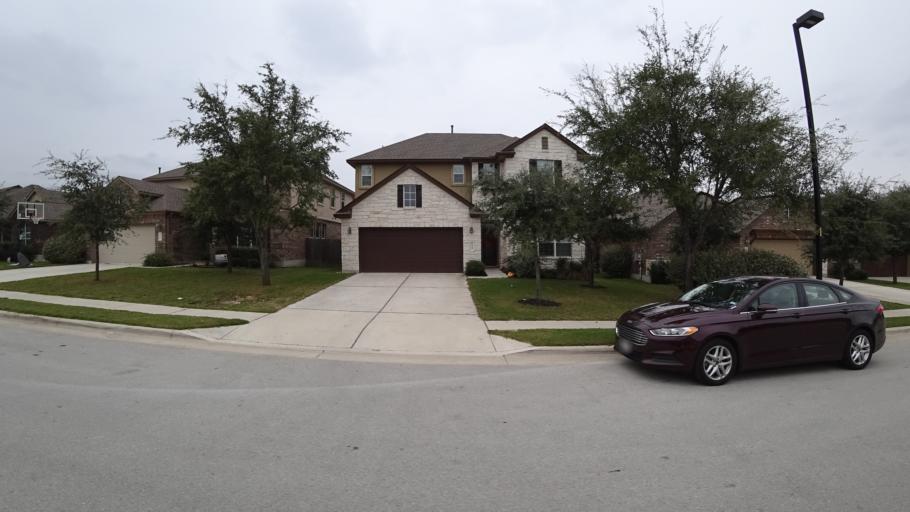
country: US
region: Texas
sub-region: Travis County
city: Shady Hollow
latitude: 30.1792
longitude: -97.9049
